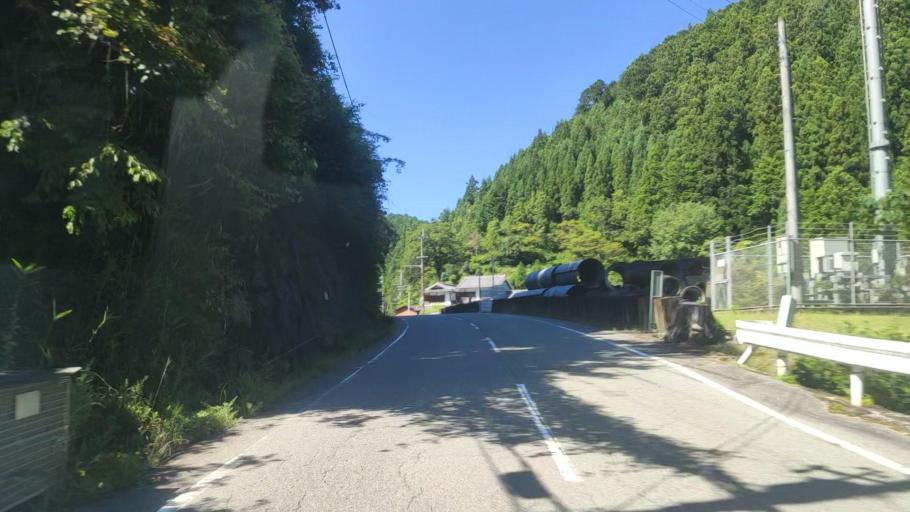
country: JP
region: Nara
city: Yoshino-cho
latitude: 34.4140
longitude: 135.9347
